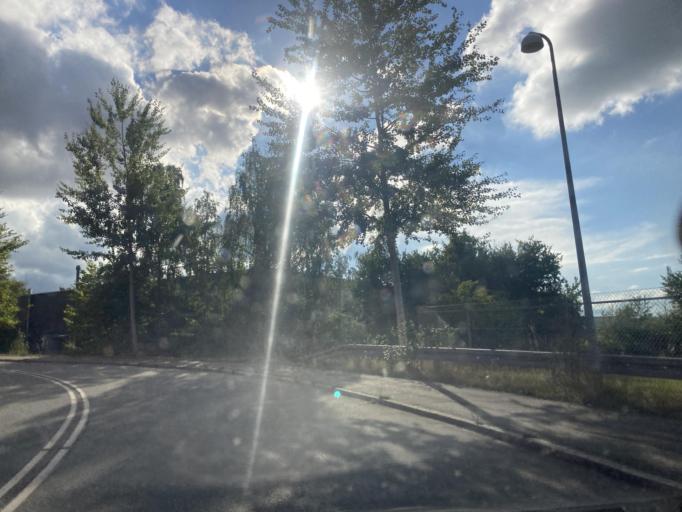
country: DK
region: Zealand
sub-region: Roskilde Kommune
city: Vindinge
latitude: 55.6470
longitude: 12.1315
